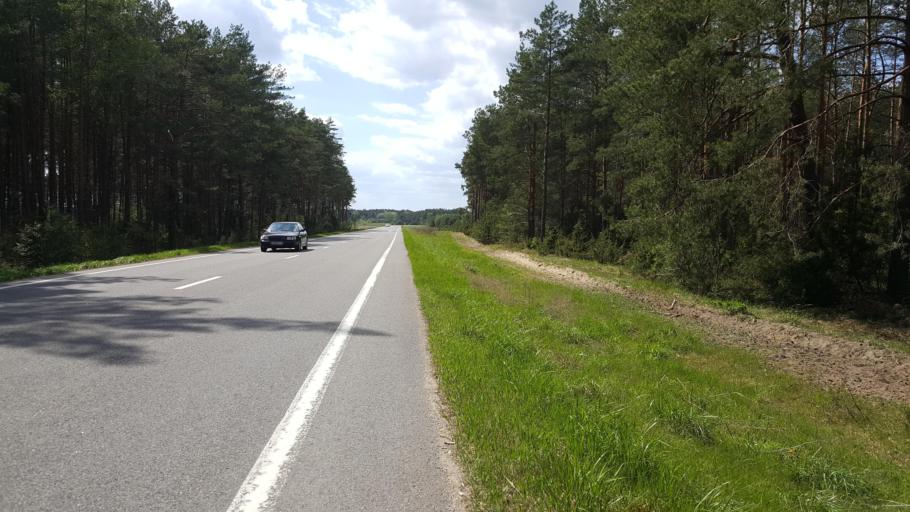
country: BY
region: Brest
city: Zhabinka
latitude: 52.3981
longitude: 24.0490
